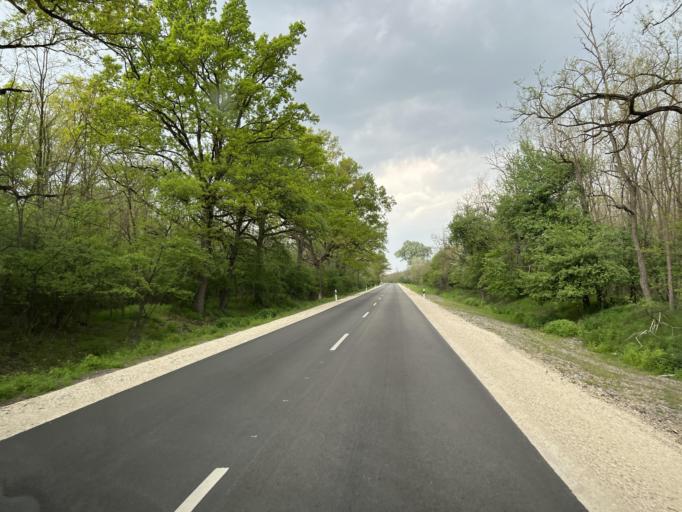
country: HU
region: Pest
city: Csemo
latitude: 47.0585
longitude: 19.7150
